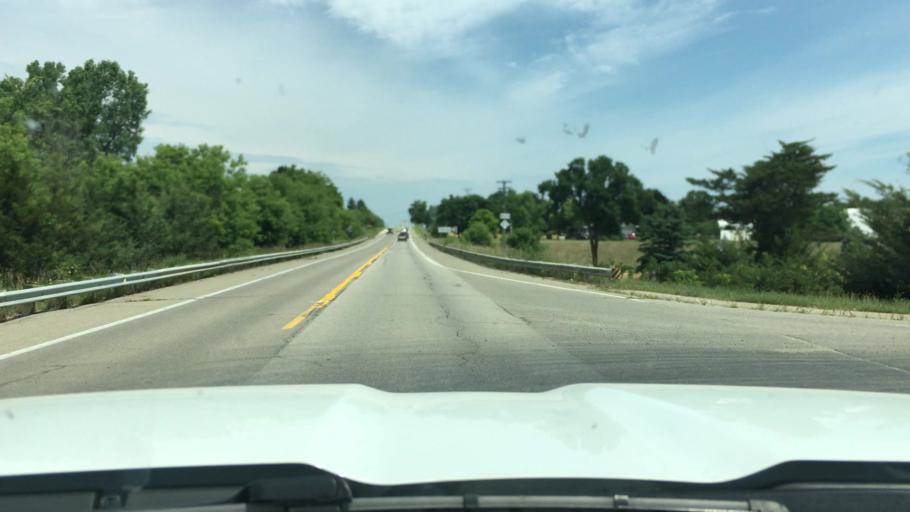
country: US
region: Michigan
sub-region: Sanilac County
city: Brown City
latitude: 43.1817
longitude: -83.0763
